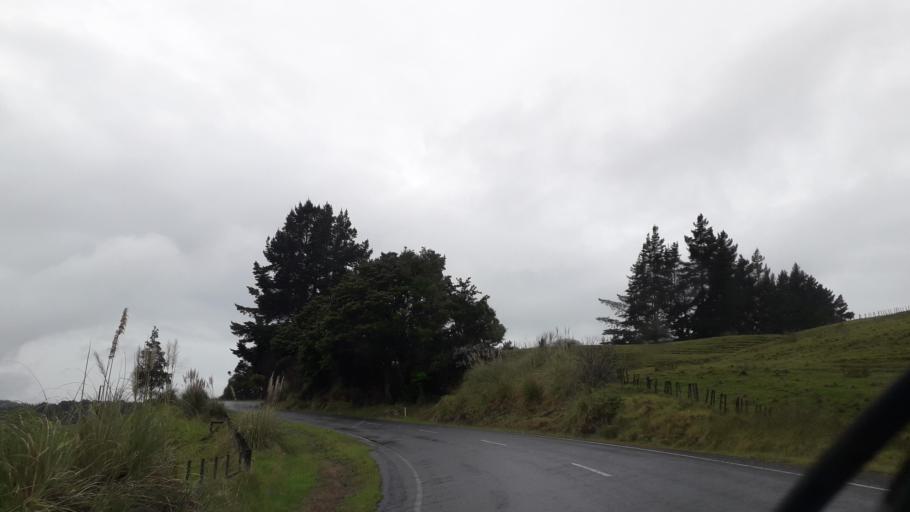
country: NZ
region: Northland
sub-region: Far North District
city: Kaitaia
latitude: -35.3594
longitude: 173.4836
